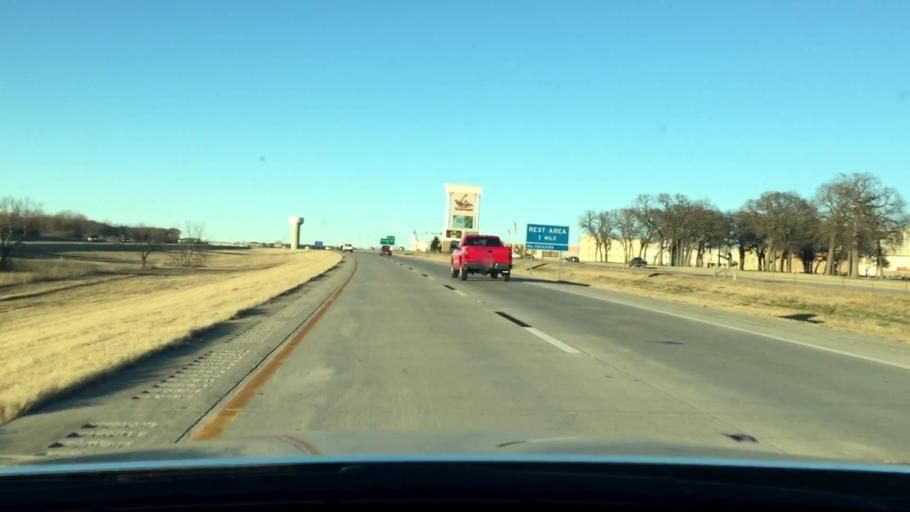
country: US
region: Texas
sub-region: Cooke County
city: Gainesville
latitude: 33.7527
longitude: -97.1351
